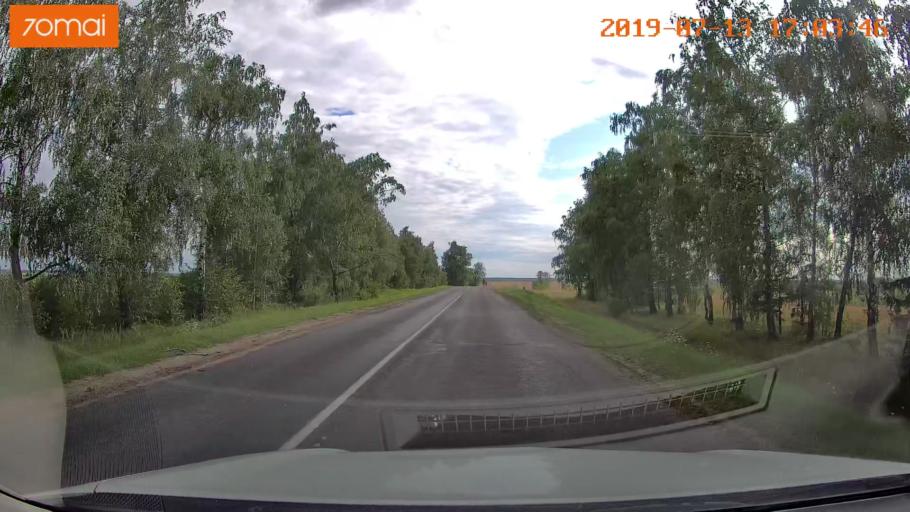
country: BY
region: Mogilev
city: Kirawsk
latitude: 53.2735
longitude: 29.3747
